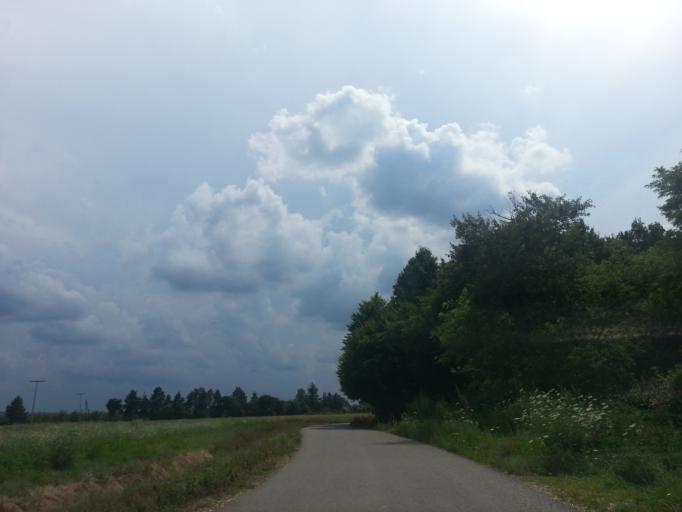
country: BA
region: Brcko
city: Brcko
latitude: 44.7788
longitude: 18.8460
